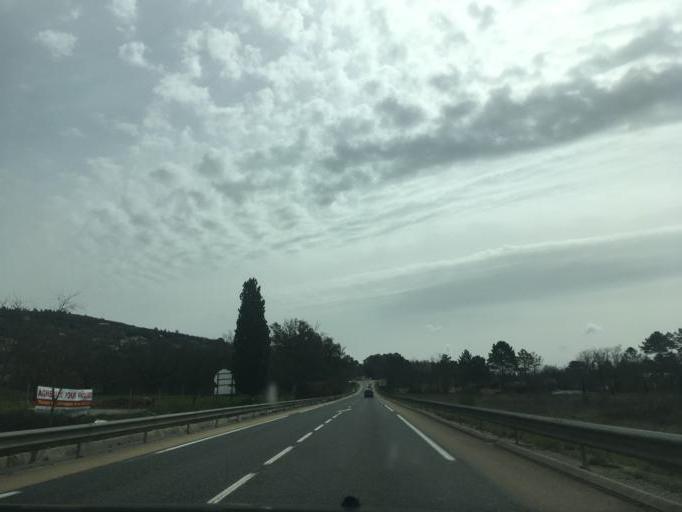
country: FR
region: Provence-Alpes-Cote d'Azur
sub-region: Departement du Var
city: Montauroux
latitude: 43.6013
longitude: 6.7803
